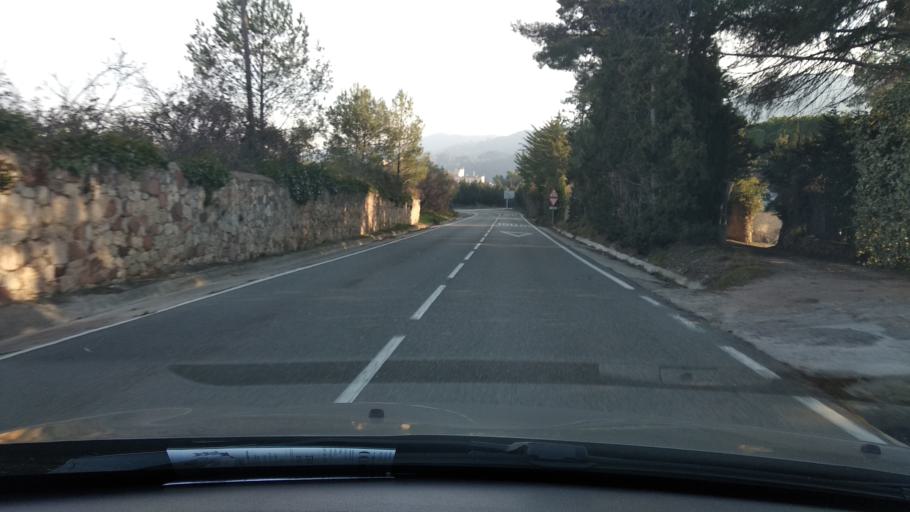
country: ES
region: Catalonia
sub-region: Provincia de Tarragona
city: Alforja
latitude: 41.2145
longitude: 0.9761
